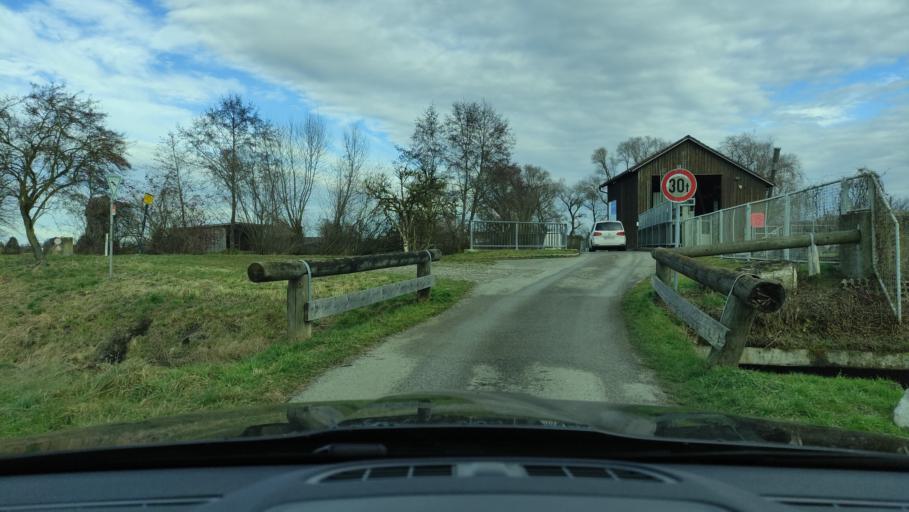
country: DE
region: Bavaria
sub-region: Swabia
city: Deisenhausen
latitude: 48.2650
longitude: 10.3200
